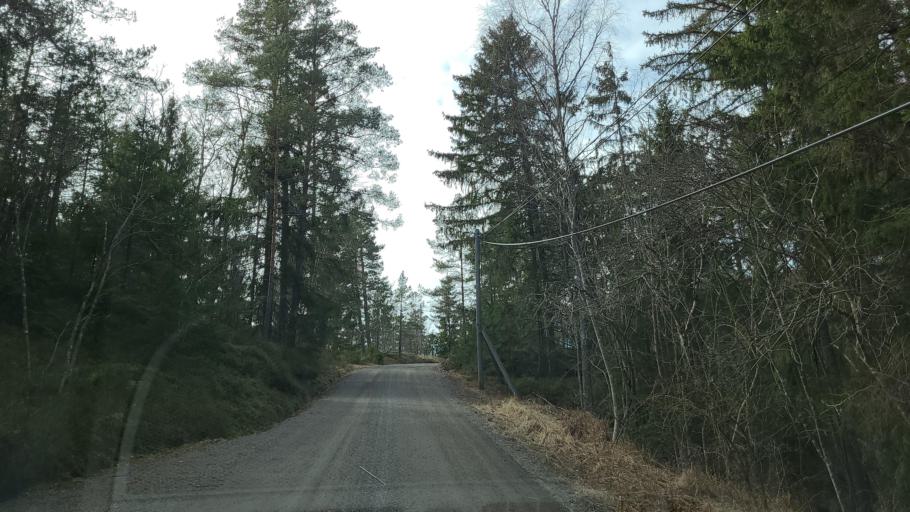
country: SE
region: Stockholm
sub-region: Varmdo Kommun
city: Hemmesta
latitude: 59.2799
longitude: 18.5466
